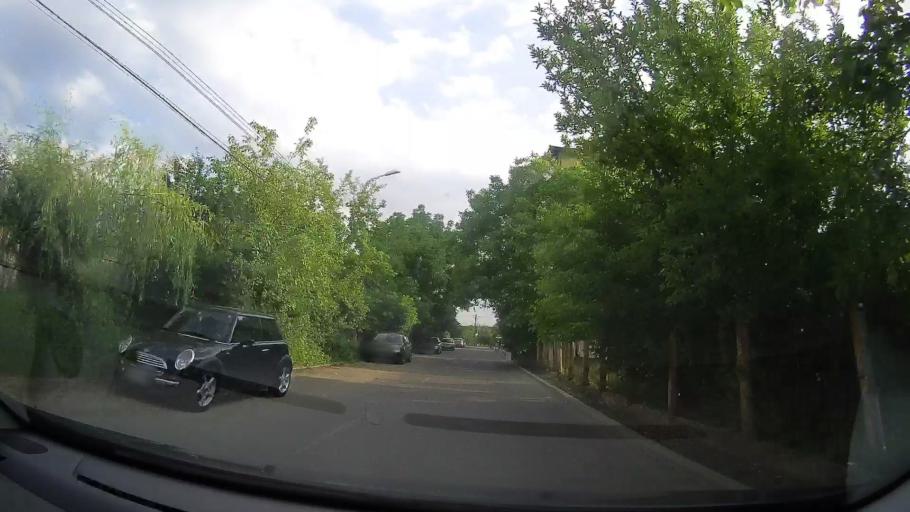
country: RO
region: Timis
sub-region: Comuna Dumbravita
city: Dumbravita
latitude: 45.7796
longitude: 21.2282
